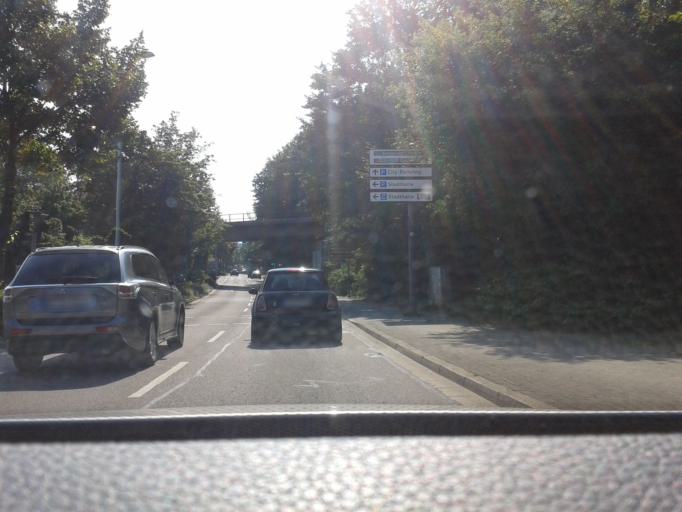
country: DE
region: North Rhine-Westphalia
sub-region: Regierungsbezirk Dusseldorf
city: Muelheim (Ruhr)
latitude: 51.4299
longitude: 6.8694
